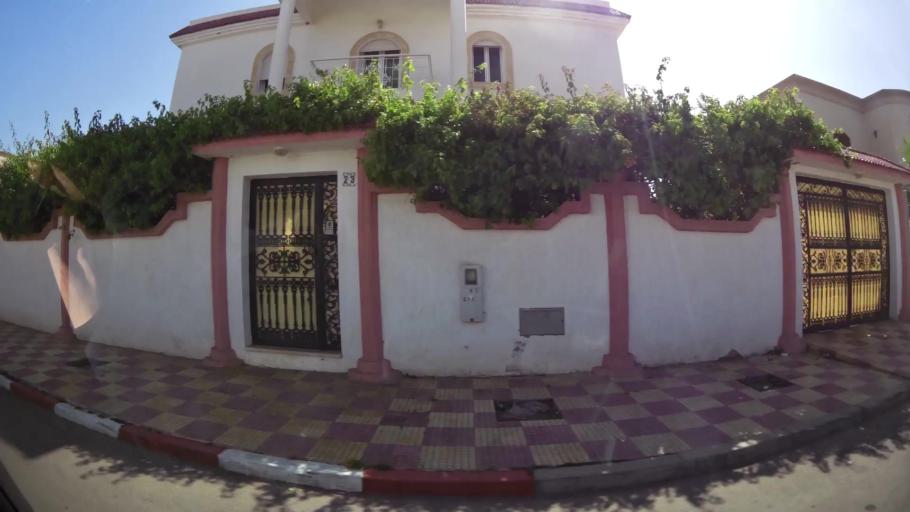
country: MA
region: Souss-Massa-Draa
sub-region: Inezgane-Ait Mellou
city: Inezgane
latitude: 30.3754
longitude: -9.5580
